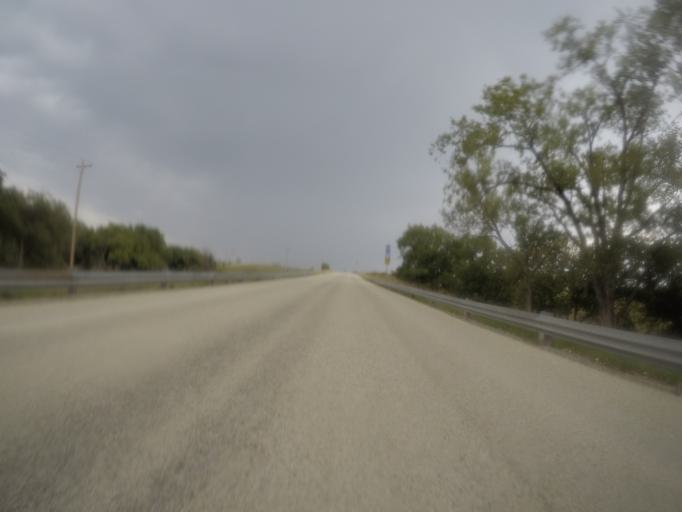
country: US
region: Kansas
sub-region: Geary County
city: Grandview Plaza
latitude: 39.0557
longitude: -96.7423
